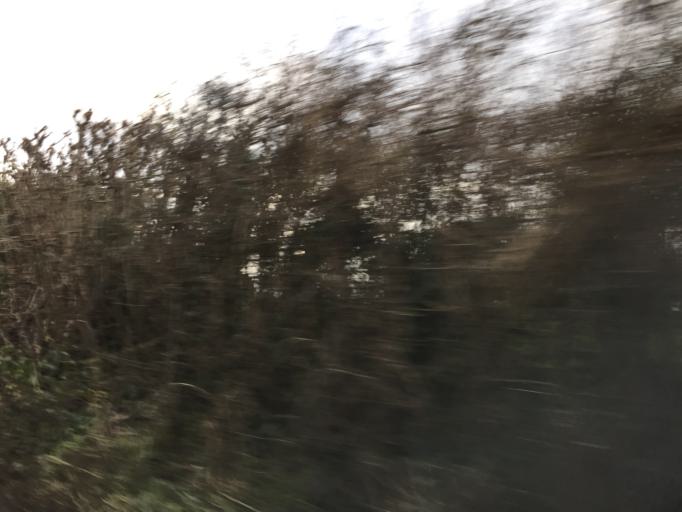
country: GB
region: Wales
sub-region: Monmouthshire
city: Rogiet
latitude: 51.5986
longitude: -2.7763
